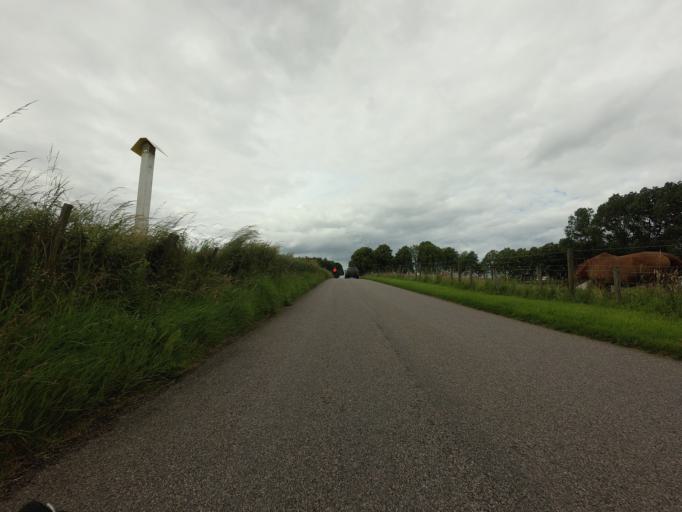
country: GB
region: Scotland
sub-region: Moray
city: Forres
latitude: 57.6005
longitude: -3.7219
